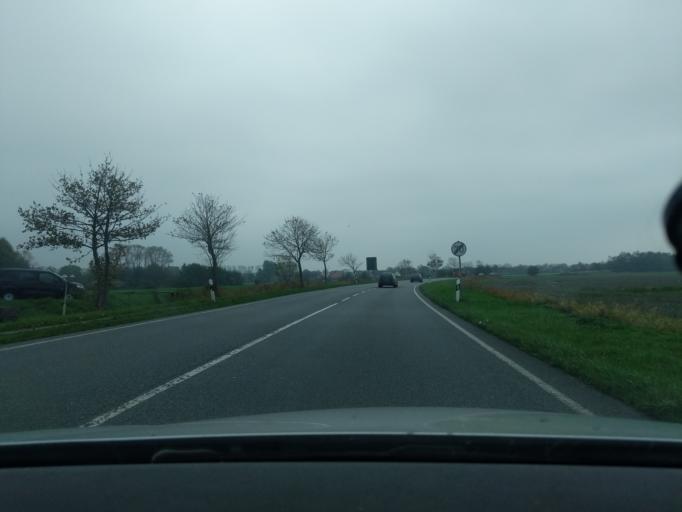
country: DE
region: Lower Saxony
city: Wanna
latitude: 53.8253
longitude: 8.7639
